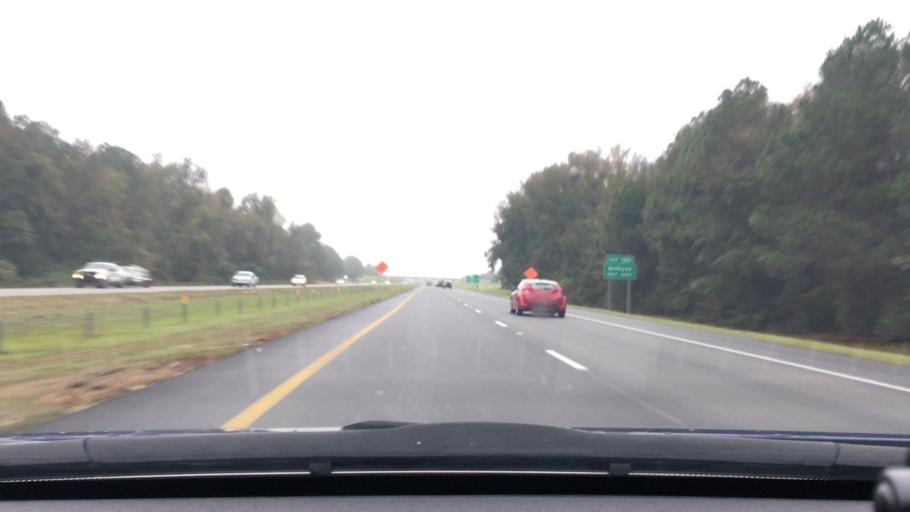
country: US
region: South Carolina
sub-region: Lee County
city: Bishopville
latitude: 34.1873
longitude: -80.2018
